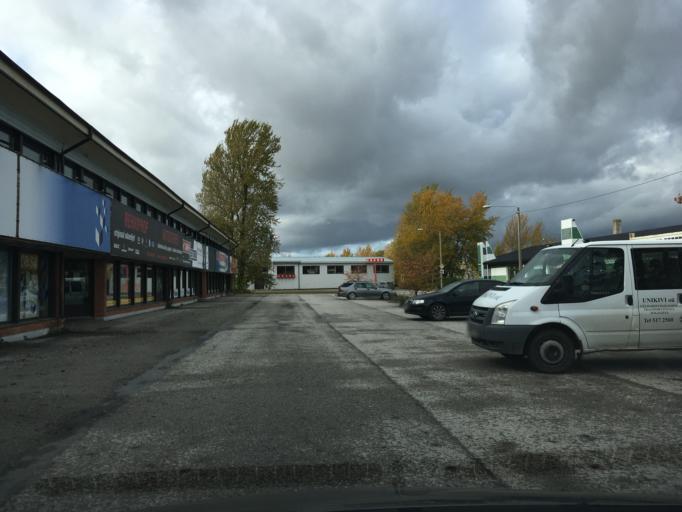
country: EE
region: Paernumaa
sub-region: Paernu linn
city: Parnu
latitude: 58.3746
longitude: 24.5492
